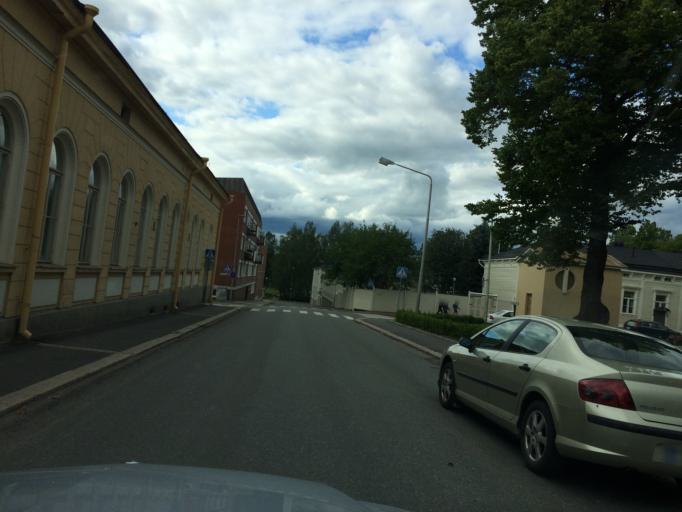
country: FI
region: Haeme
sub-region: Haemeenlinna
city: Haemeenlinna
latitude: 60.9989
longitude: 24.4618
